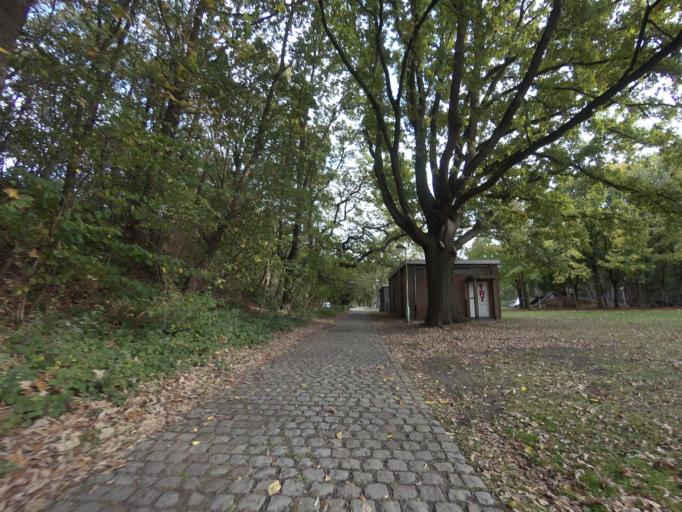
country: BE
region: Flanders
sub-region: Provincie Antwerpen
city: Brasschaat
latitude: 51.2644
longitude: 4.4572
